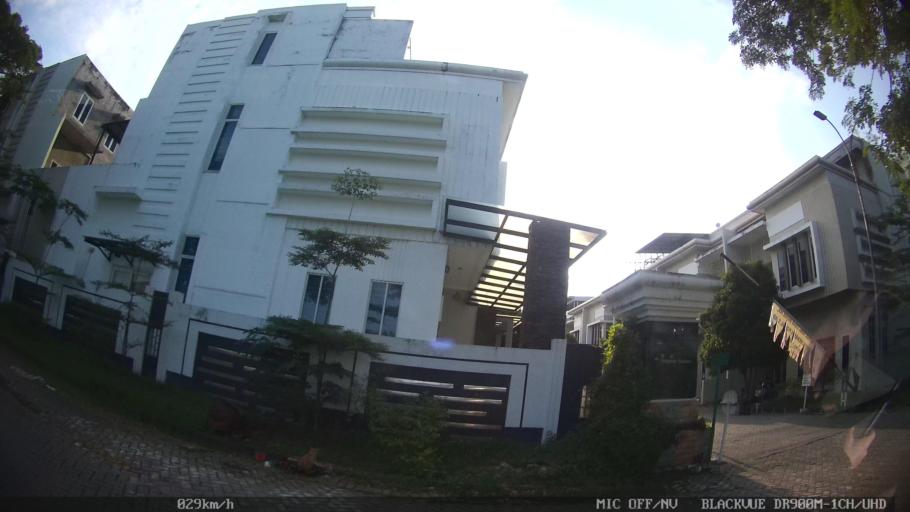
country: ID
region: North Sumatra
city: Medan
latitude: 3.6229
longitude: 98.6431
